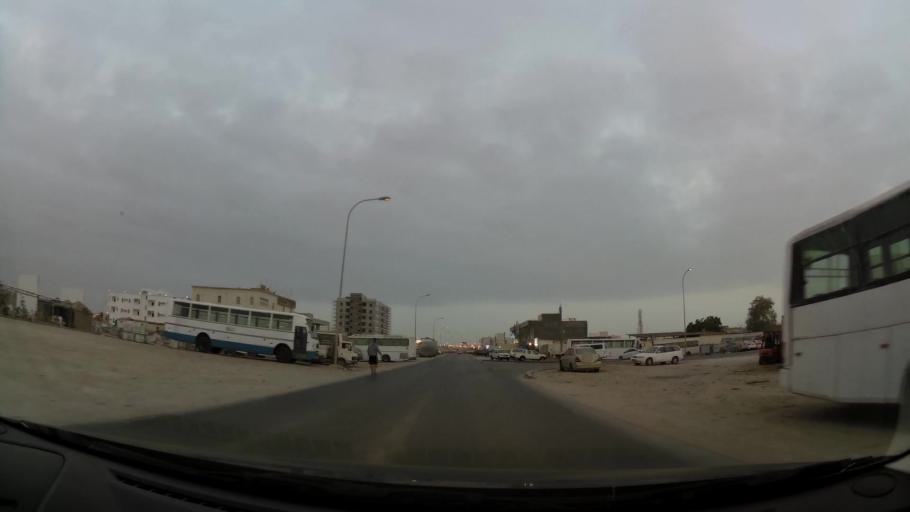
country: OM
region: Zufar
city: Salalah
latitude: 17.0255
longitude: 54.0541
